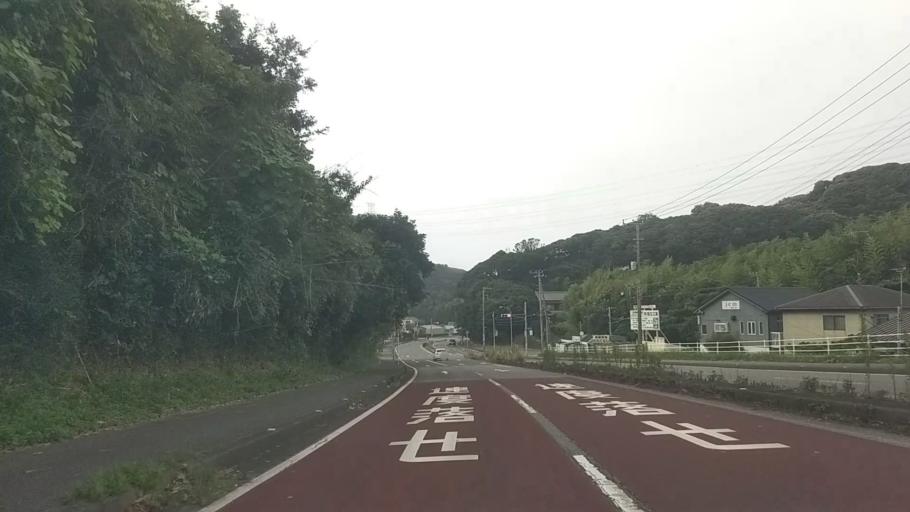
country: JP
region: Chiba
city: Kimitsu
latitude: 35.3412
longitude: 139.8915
